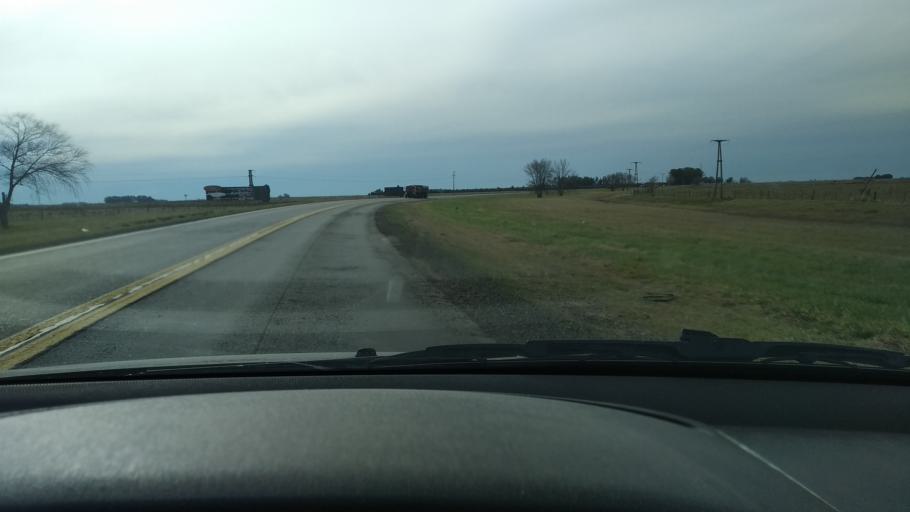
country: AR
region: Buenos Aires
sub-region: Partido de Azul
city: Azul
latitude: -36.7531
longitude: -59.8045
